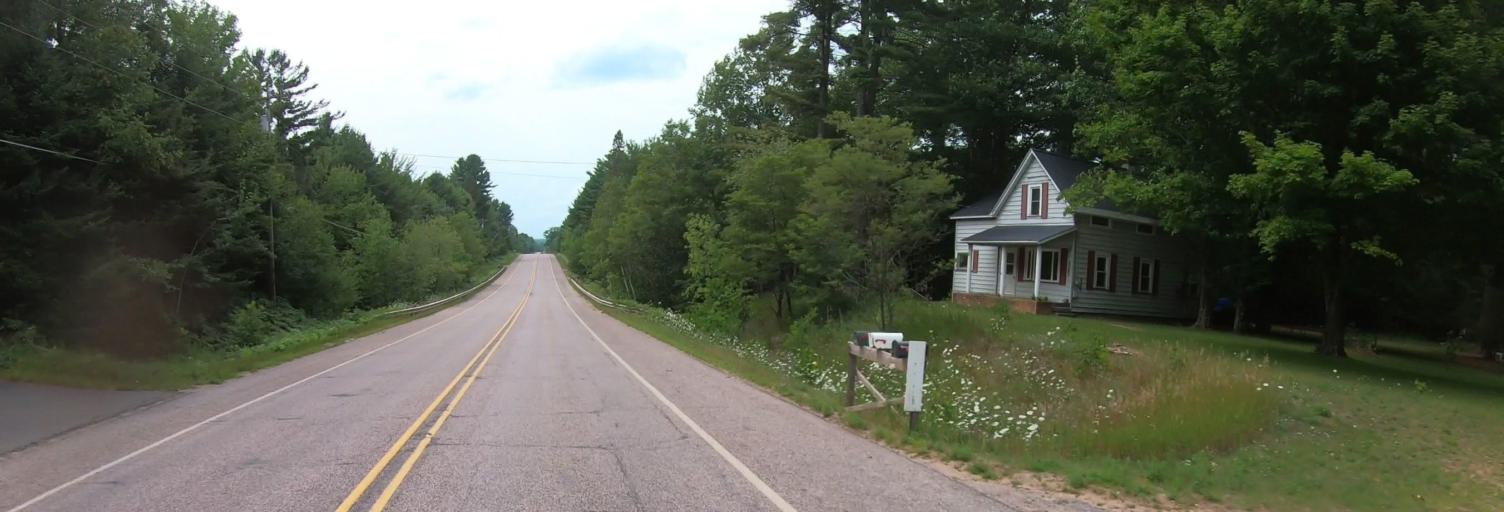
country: US
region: Michigan
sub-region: Marquette County
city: Harvey
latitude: 46.4631
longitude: -87.3470
